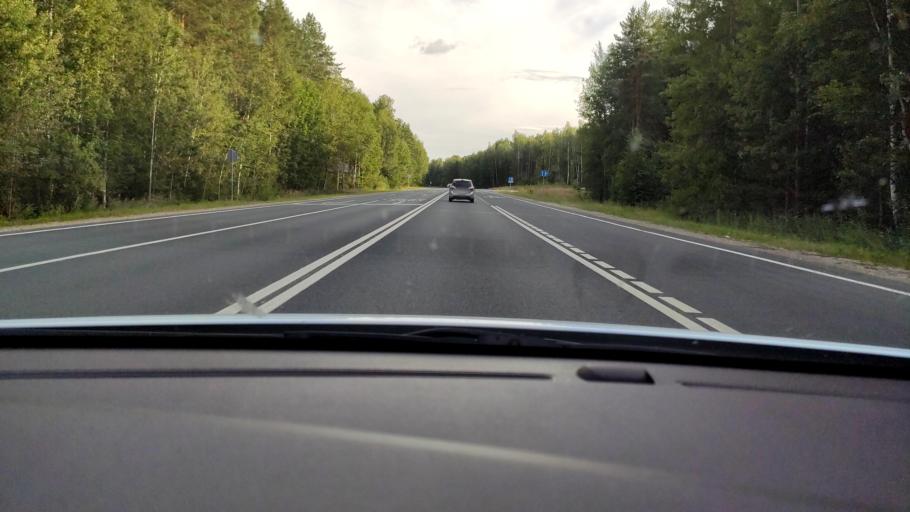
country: RU
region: Mariy-El
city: Suslonger
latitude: 56.2405
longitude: 48.2319
